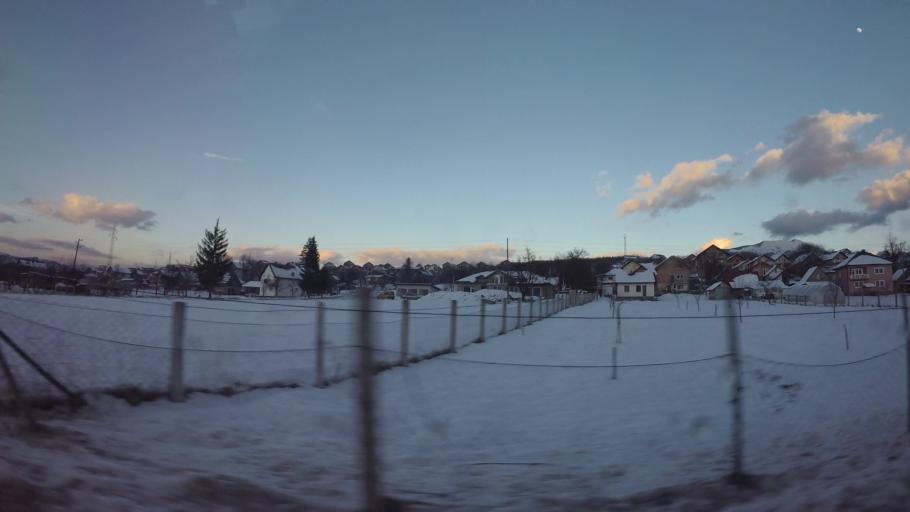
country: BA
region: Federation of Bosnia and Herzegovina
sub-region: Kanton Sarajevo
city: Sarajevo
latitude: 43.8100
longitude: 18.3736
